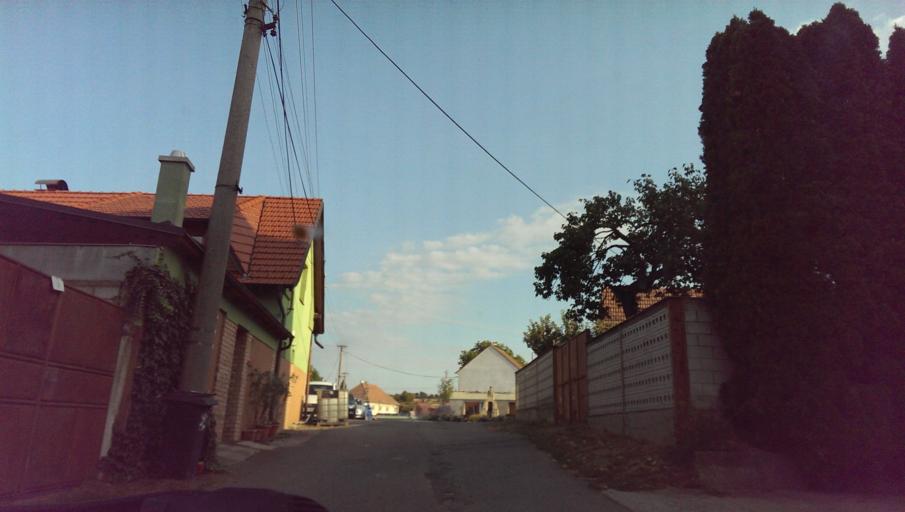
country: CZ
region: South Moravian
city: Zeravice
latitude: 49.0502
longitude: 17.2709
